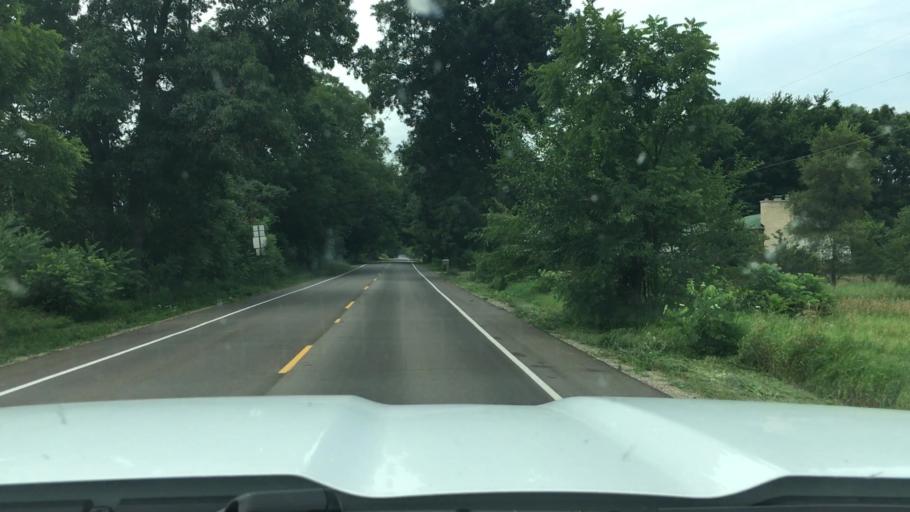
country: US
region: Michigan
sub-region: Allegan County
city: Plainwell
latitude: 42.4638
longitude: -85.6027
